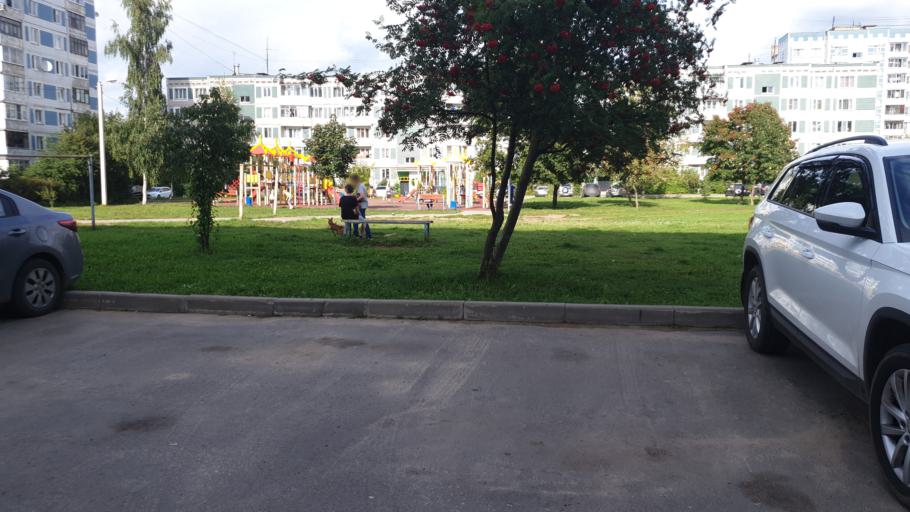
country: RU
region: Moskovskaya
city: Yakhroma
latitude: 56.2860
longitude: 37.4885
